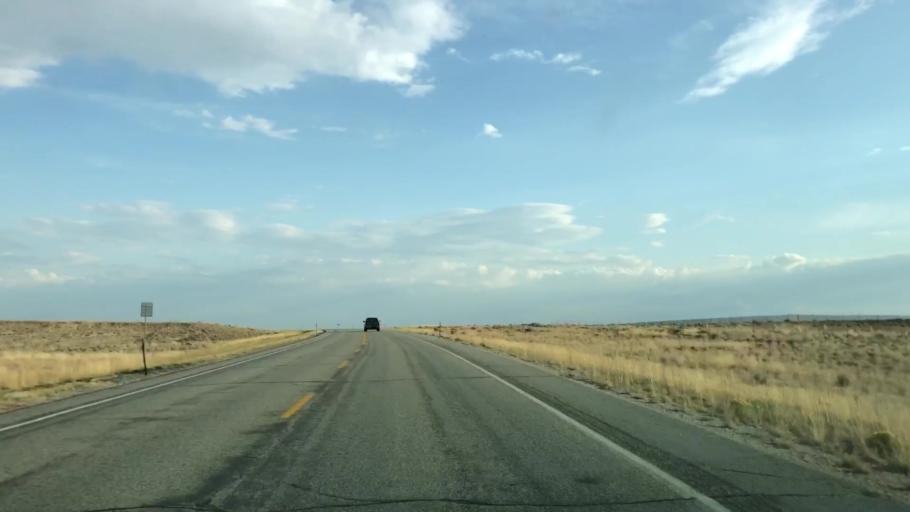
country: US
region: Wyoming
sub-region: Sublette County
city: Marbleton
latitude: 42.3420
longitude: -109.5219
